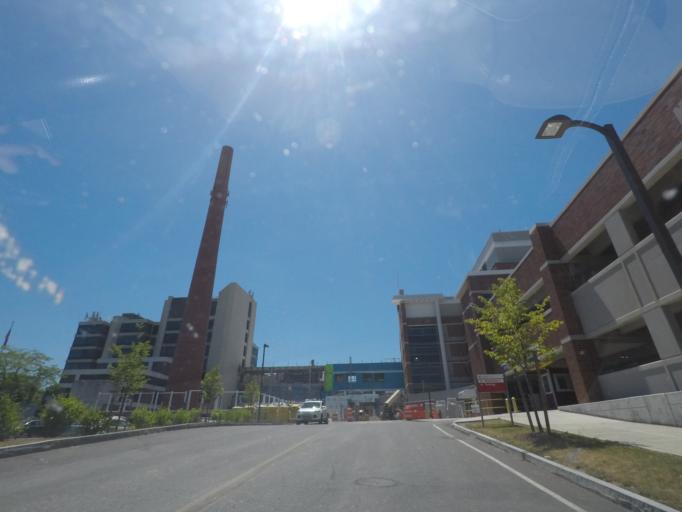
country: US
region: New York
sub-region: Rensselaer County
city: Troy
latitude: 42.7345
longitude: -73.6726
